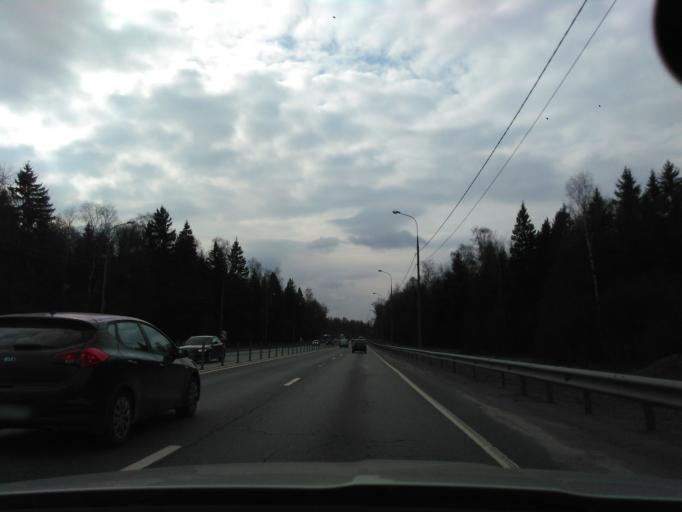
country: RU
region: Moskovskaya
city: Marfino
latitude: 56.0400
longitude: 37.5418
